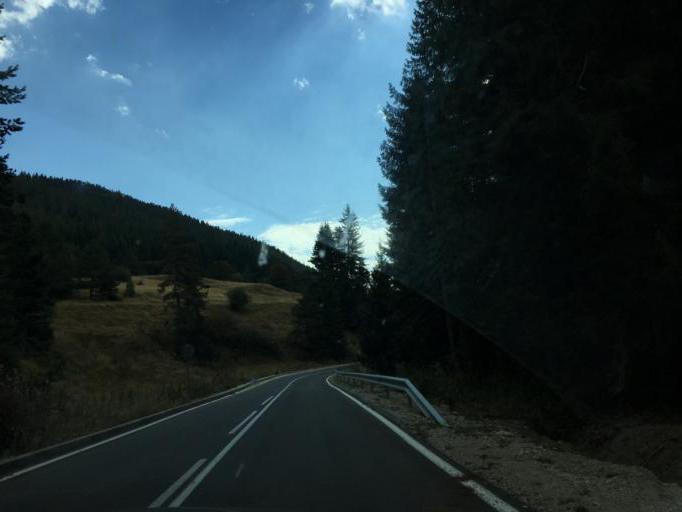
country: BG
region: Pazardzhik
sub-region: Obshtina Batak
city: Batak
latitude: 41.9008
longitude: 24.3117
